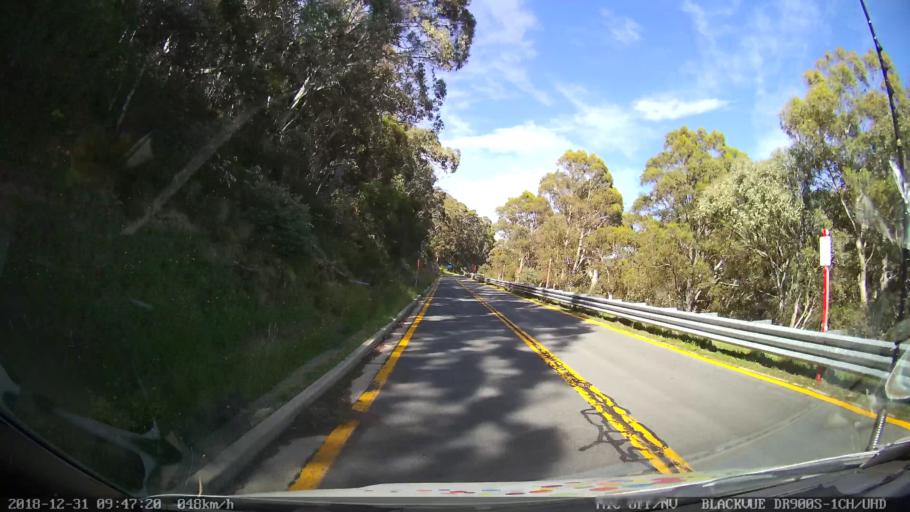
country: AU
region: New South Wales
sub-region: Snowy River
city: Jindabyne
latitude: -36.5080
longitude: 148.3025
